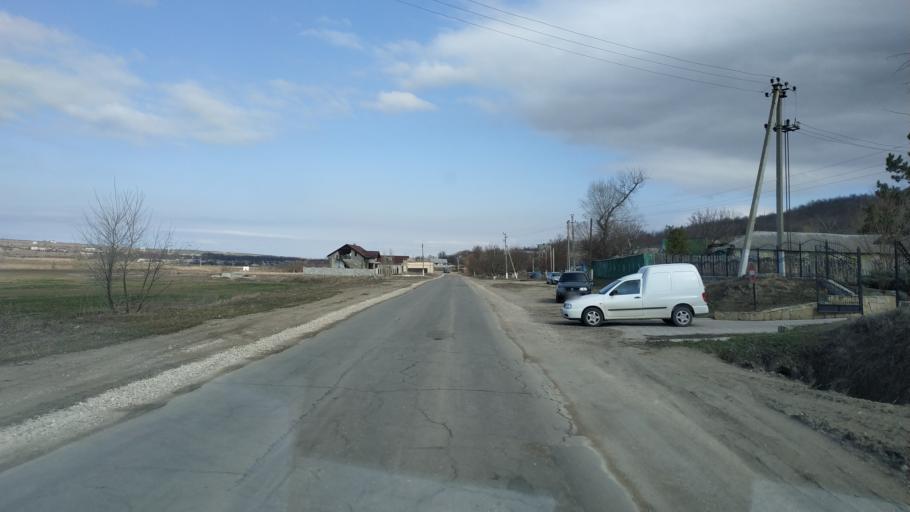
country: MD
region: Causeni
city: Causeni
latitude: 46.6395
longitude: 29.3814
